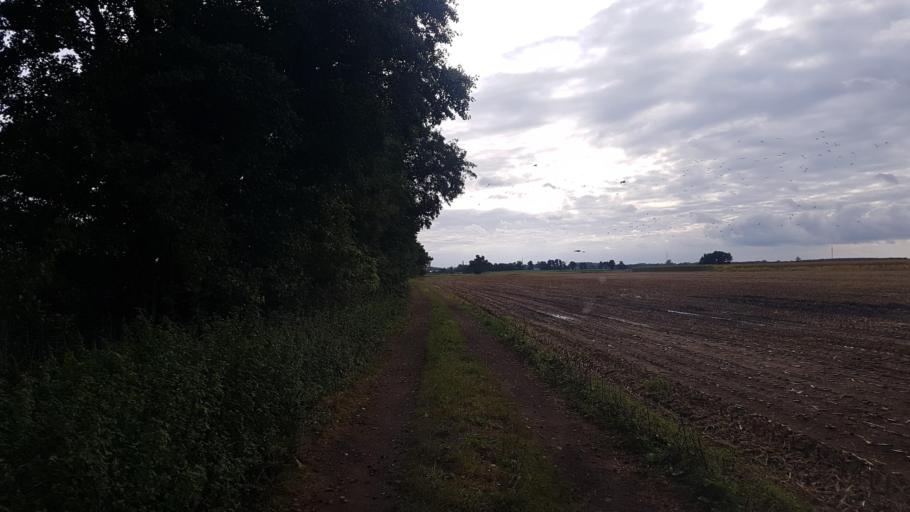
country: DE
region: Brandenburg
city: Bad Liebenwerda
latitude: 51.4835
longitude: 13.4053
